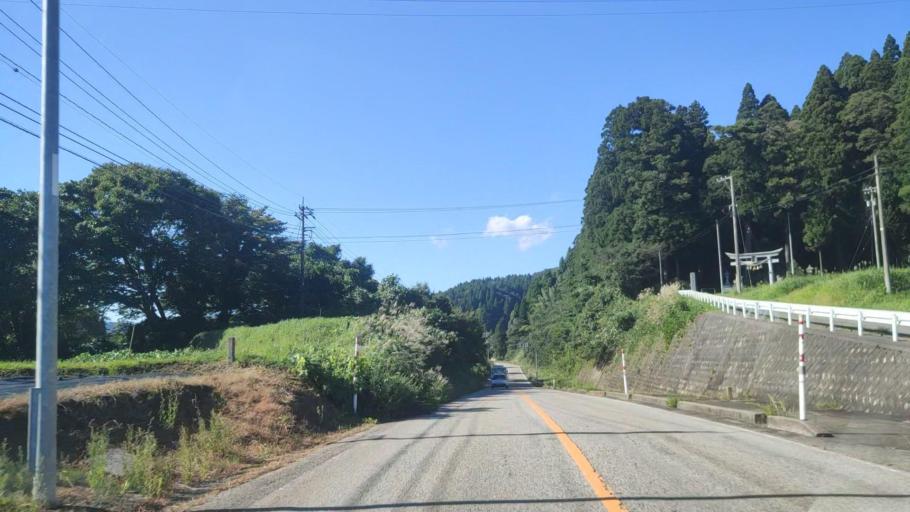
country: JP
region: Ishikawa
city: Nanao
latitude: 37.2741
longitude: 137.0547
